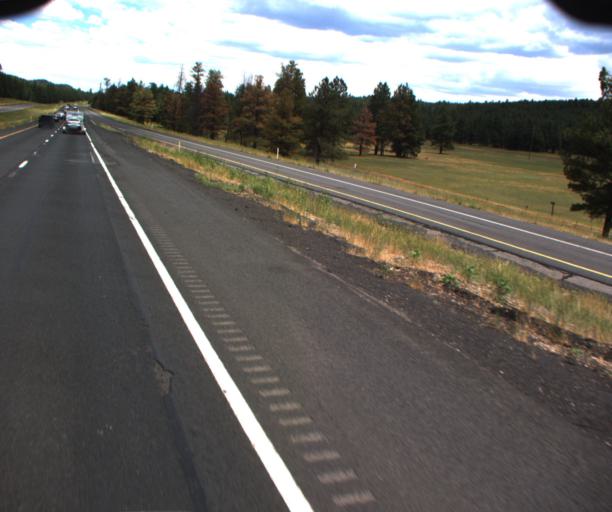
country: US
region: Arizona
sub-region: Coconino County
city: Mountainaire
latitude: 34.9831
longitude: -111.6861
